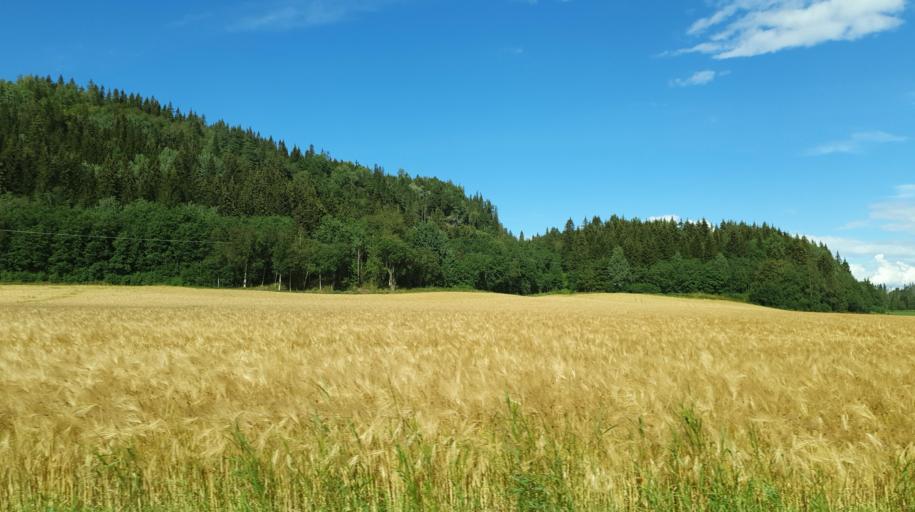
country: NO
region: Nord-Trondelag
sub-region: Levanger
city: Levanger
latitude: 63.6976
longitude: 11.2625
